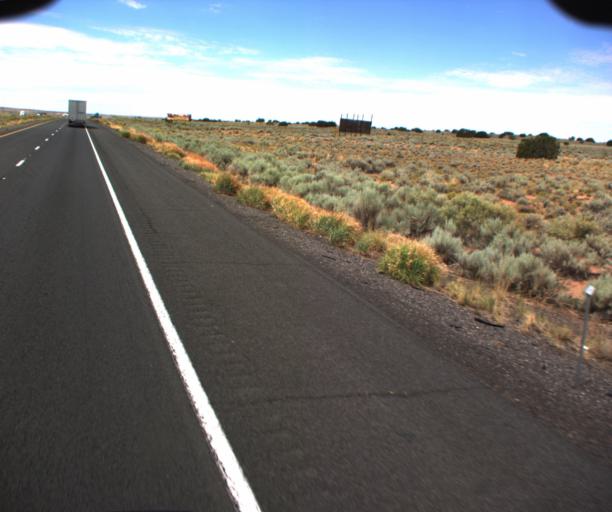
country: US
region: Arizona
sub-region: Apache County
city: Houck
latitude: 35.1416
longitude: -109.5217
